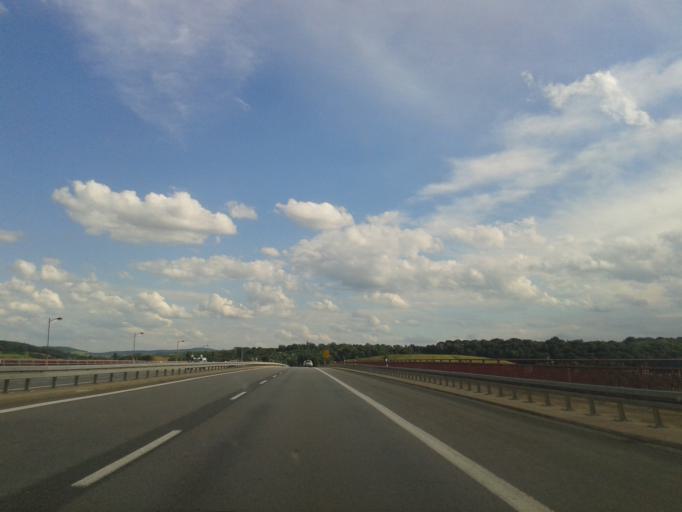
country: DE
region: Saxony
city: Pirna
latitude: 50.9643
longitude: 13.9156
